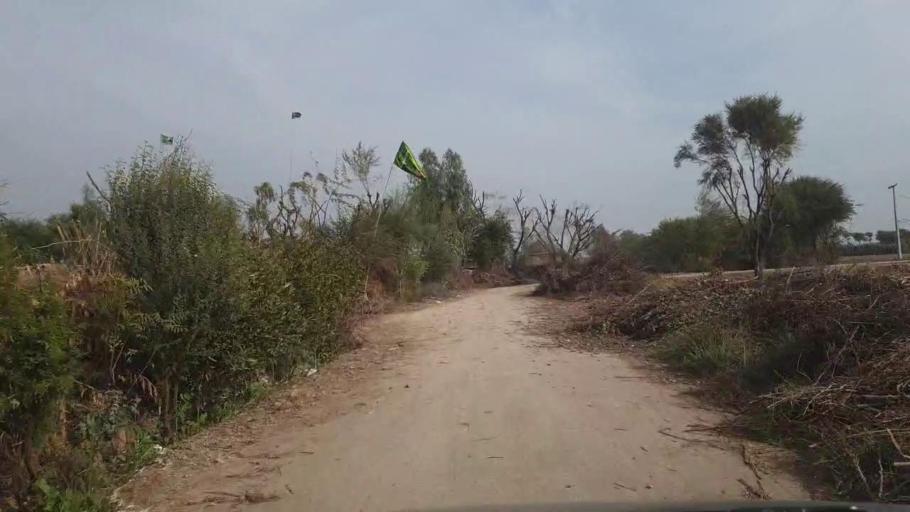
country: PK
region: Sindh
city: Shahpur Chakar
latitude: 26.0907
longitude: 68.4898
